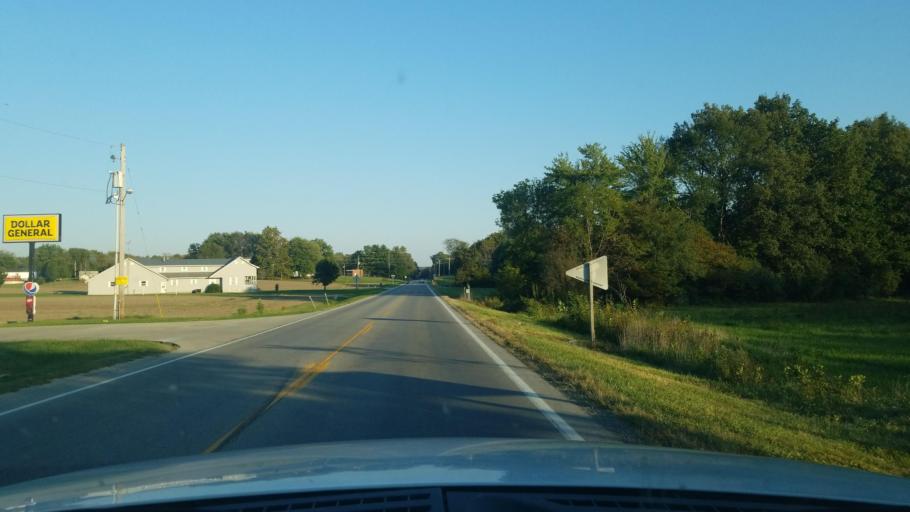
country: US
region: Illinois
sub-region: Saline County
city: Harrisburg
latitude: 37.8395
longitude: -88.6008
